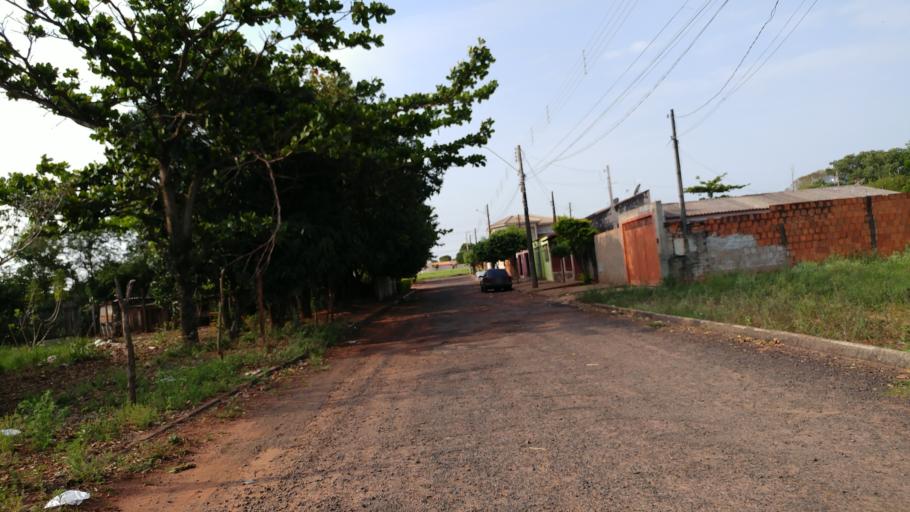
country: BR
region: Sao Paulo
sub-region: Paraguacu Paulista
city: Paraguacu Paulista
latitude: -22.4189
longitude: -50.5898
